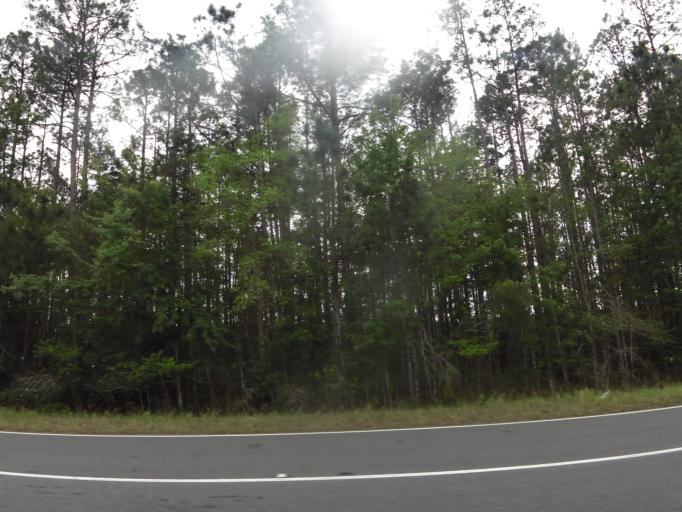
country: US
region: Georgia
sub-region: Charlton County
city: Folkston
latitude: 30.8359
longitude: -81.8902
